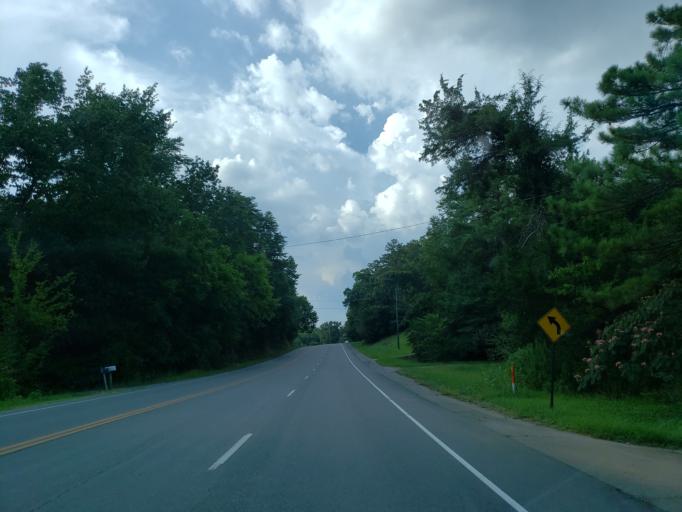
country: US
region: Georgia
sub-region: Polk County
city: Rockmart
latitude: 33.9756
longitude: -85.0331
